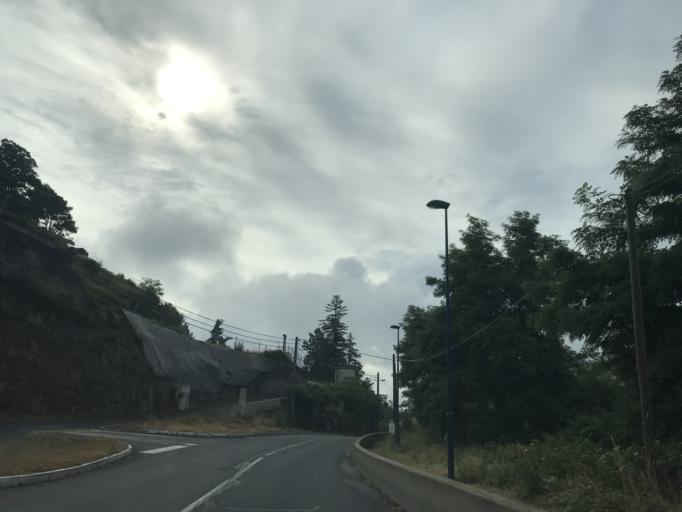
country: FR
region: Auvergne
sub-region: Departement de la Haute-Loire
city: Espaly-Saint-Marcel
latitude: 45.0539
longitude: 3.8539
